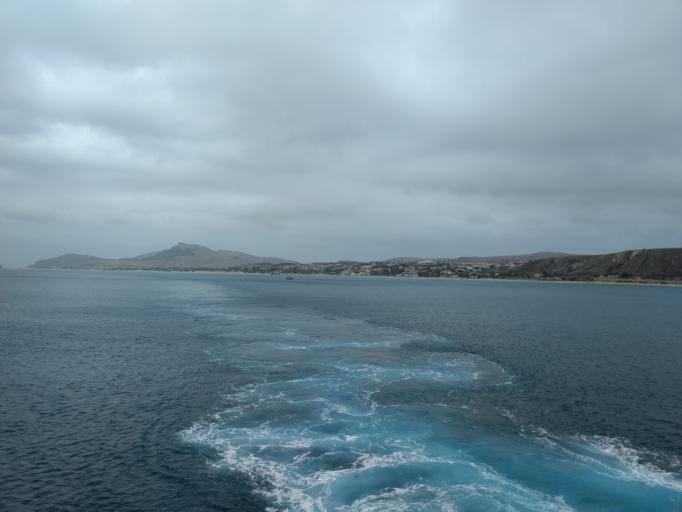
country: PT
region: Madeira
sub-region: Porto Santo
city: Vila de Porto Santo
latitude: 33.0587
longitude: -16.3146
